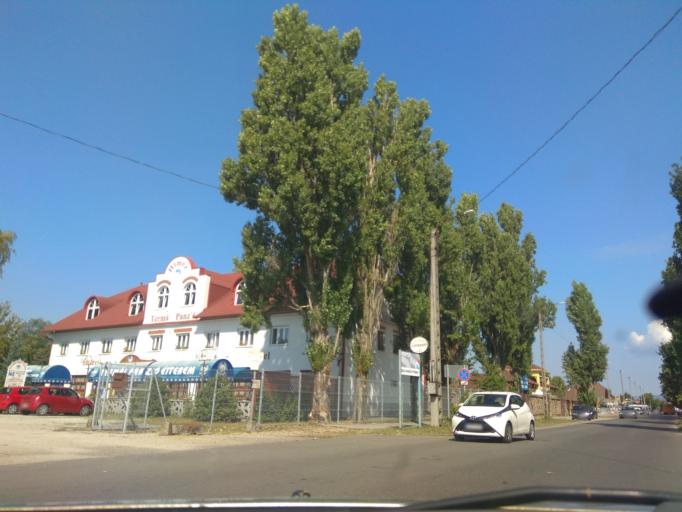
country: HU
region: Heves
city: Szihalom
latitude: 47.7933
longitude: 20.5245
